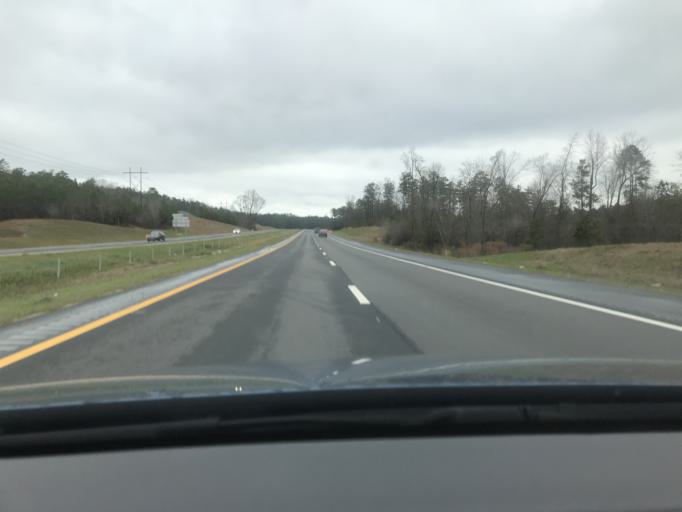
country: US
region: North Carolina
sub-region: Cumberland County
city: Fort Bragg
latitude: 35.0826
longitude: -79.0221
